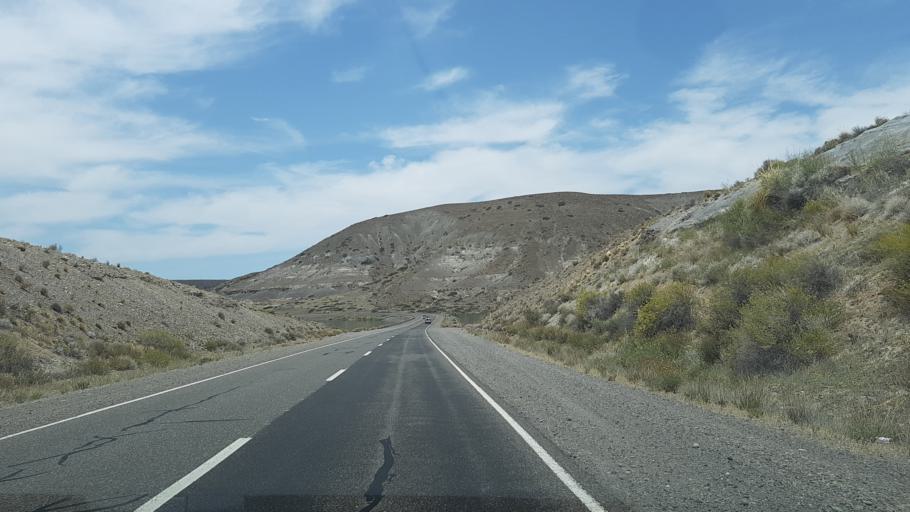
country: AR
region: Neuquen
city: Junin de los Andes
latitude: -40.4540
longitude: -70.6648
